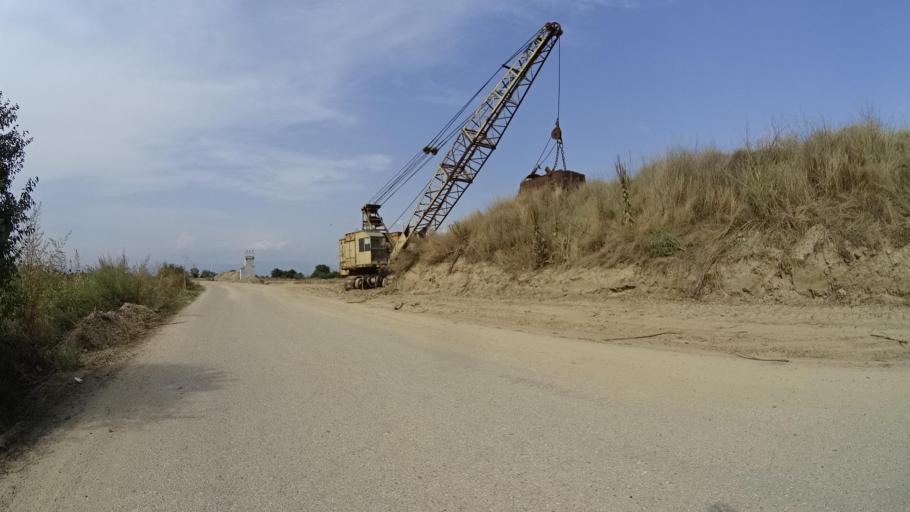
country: BG
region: Plovdiv
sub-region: Obshtina Kaloyanovo
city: Kaloyanovo
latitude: 42.3119
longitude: 24.7997
